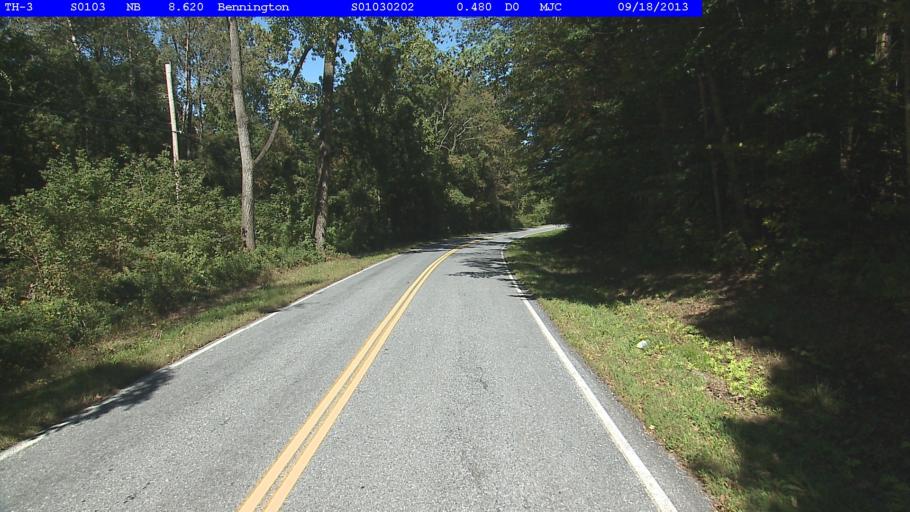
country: US
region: Vermont
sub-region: Bennington County
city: Bennington
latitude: 42.8436
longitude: -73.1726
